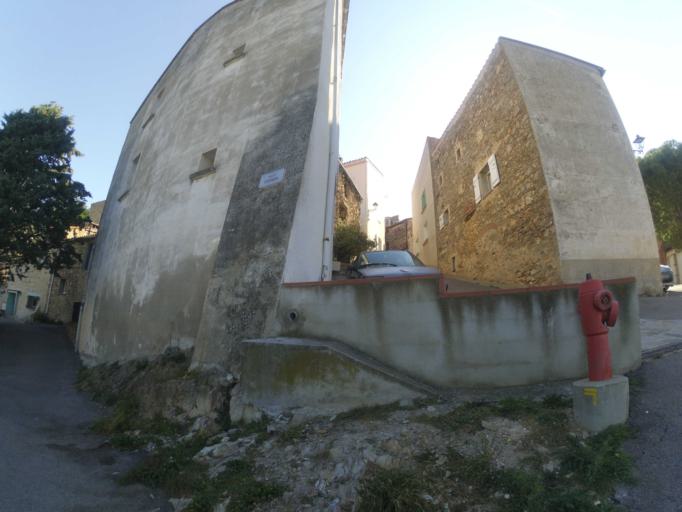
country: FR
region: Languedoc-Roussillon
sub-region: Departement des Pyrenees-Orientales
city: Baixas
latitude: 42.7589
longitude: 2.7531
